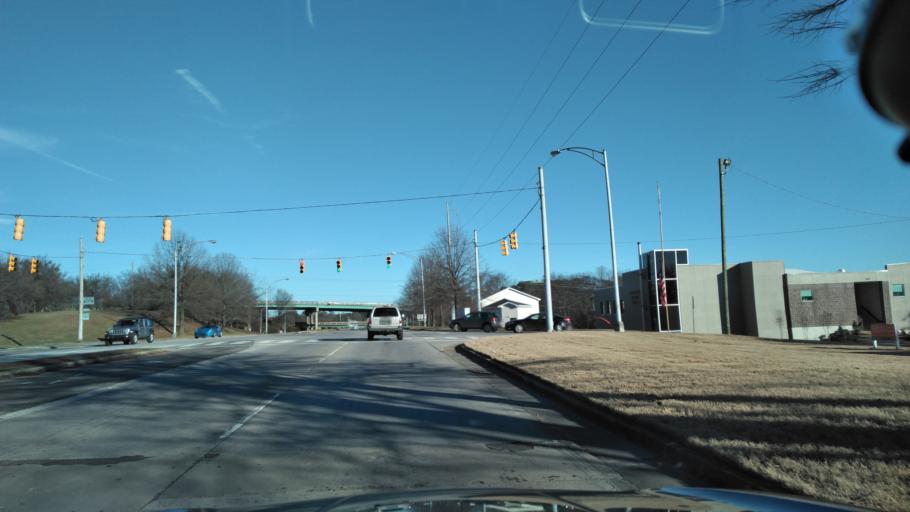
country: US
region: Alabama
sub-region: Jefferson County
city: Homewood
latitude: 33.4841
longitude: -86.7902
